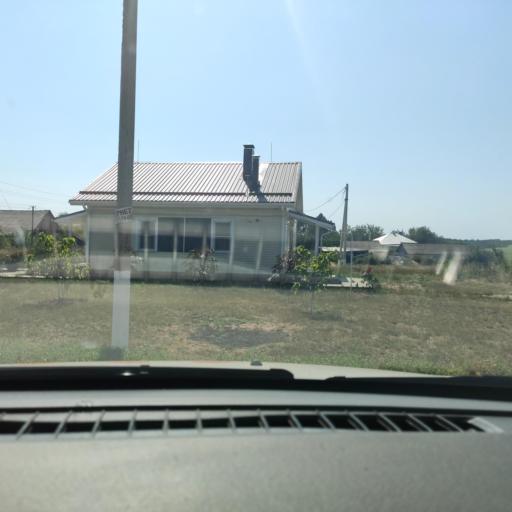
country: RU
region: Voronezj
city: Ostrogozhsk
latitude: 50.7066
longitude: 39.3329
